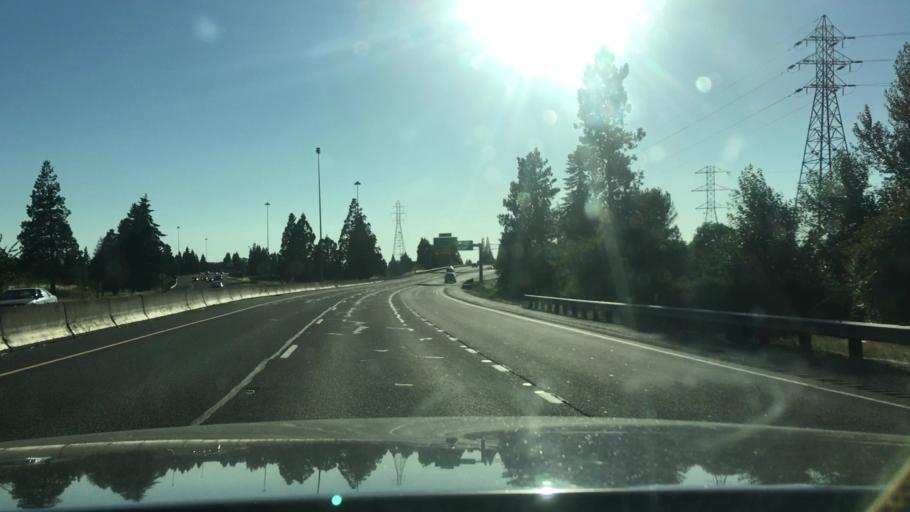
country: US
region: Oregon
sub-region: Lane County
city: Springfield
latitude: 44.0632
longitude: -123.0407
